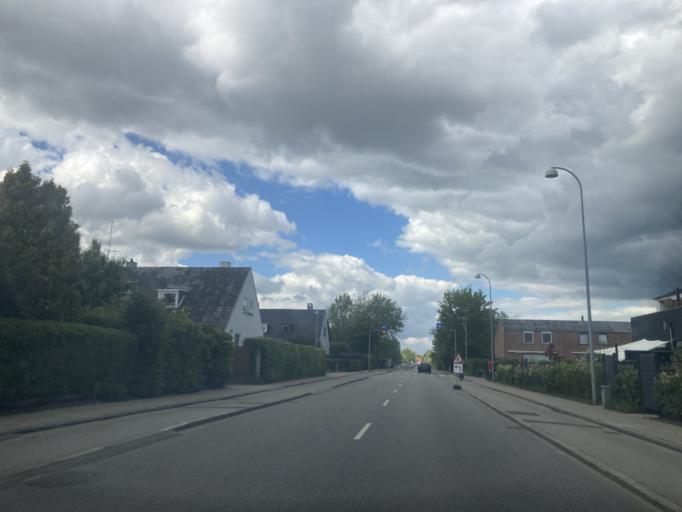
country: DK
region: Capital Region
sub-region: Gladsaxe Municipality
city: Buddinge
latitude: 55.7585
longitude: 12.4841
